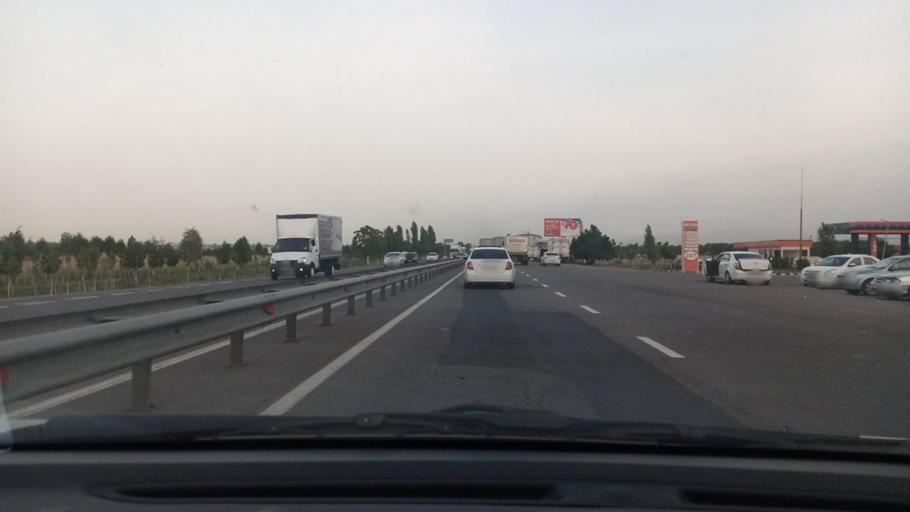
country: UZ
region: Toshkent
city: Ohangaron
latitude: 40.9193
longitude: 69.5996
